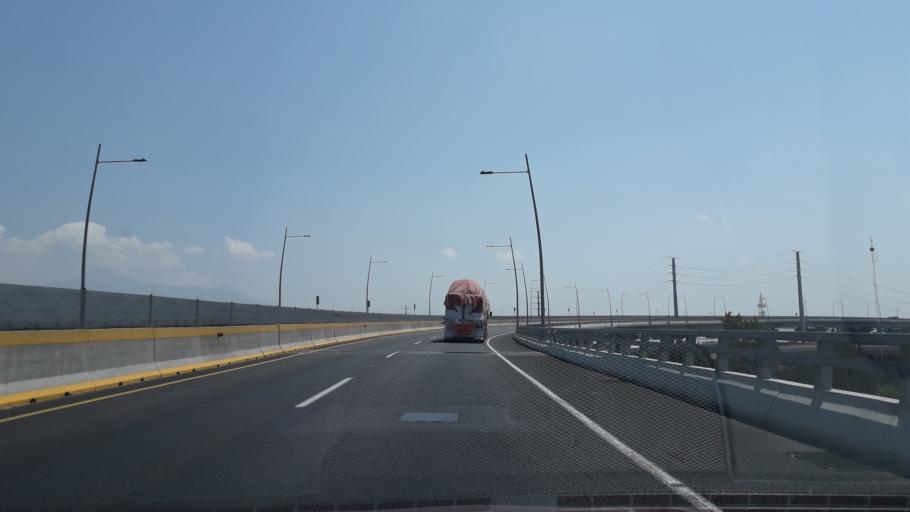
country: MX
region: Puebla
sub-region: Puebla
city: San Sebastian de Aparicio
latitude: 19.0822
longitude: -98.1679
